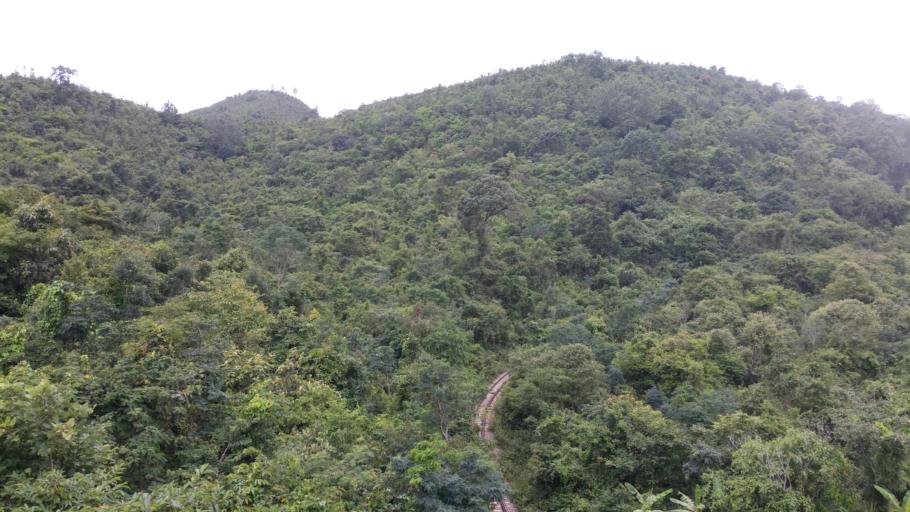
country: MM
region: Shan
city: Taunggyi
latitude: 20.7329
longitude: 96.8658
